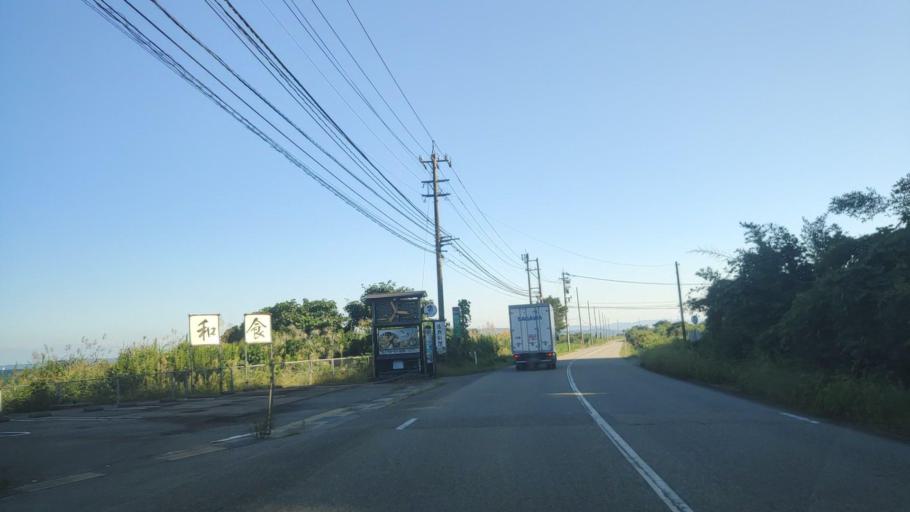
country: JP
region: Ishikawa
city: Nanao
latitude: 37.1985
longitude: 136.9096
